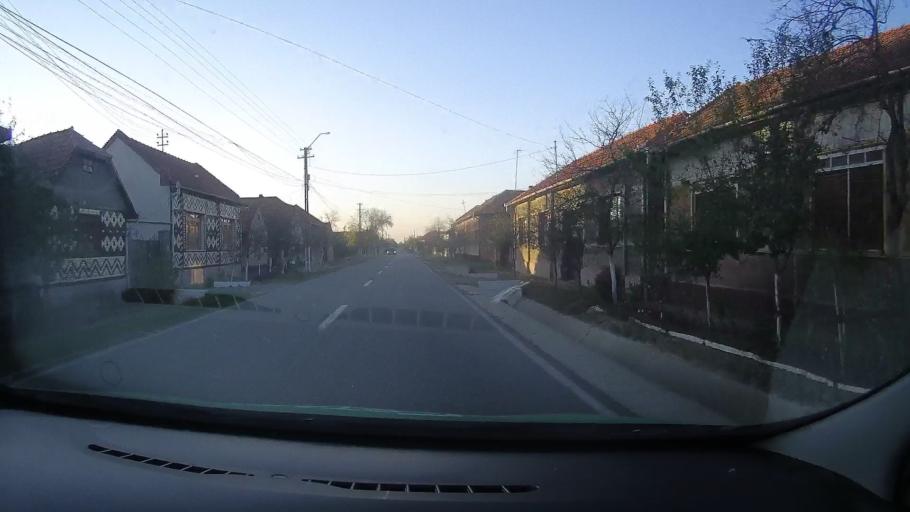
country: RO
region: Timis
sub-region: Comuna Traian Vuia
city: Traian Vuia
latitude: 45.7944
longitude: 22.0700
